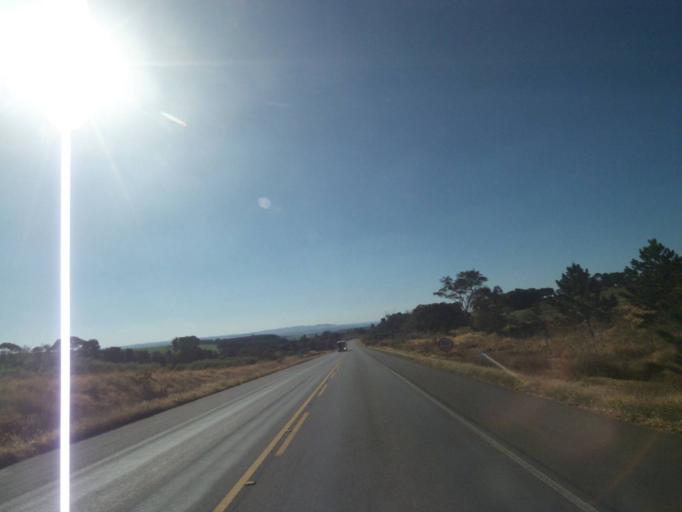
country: BR
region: Parana
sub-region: Tibagi
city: Tibagi
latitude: -24.7613
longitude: -50.4700
